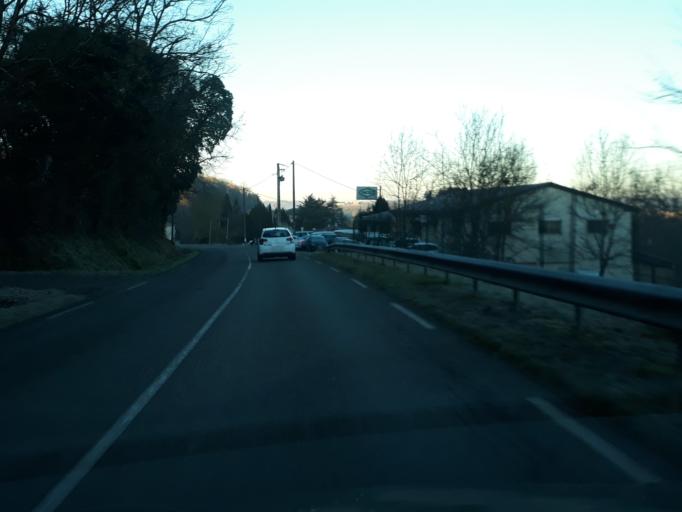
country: FR
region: Midi-Pyrenees
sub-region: Departement du Gers
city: Pavie
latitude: 43.6299
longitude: 0.6206
